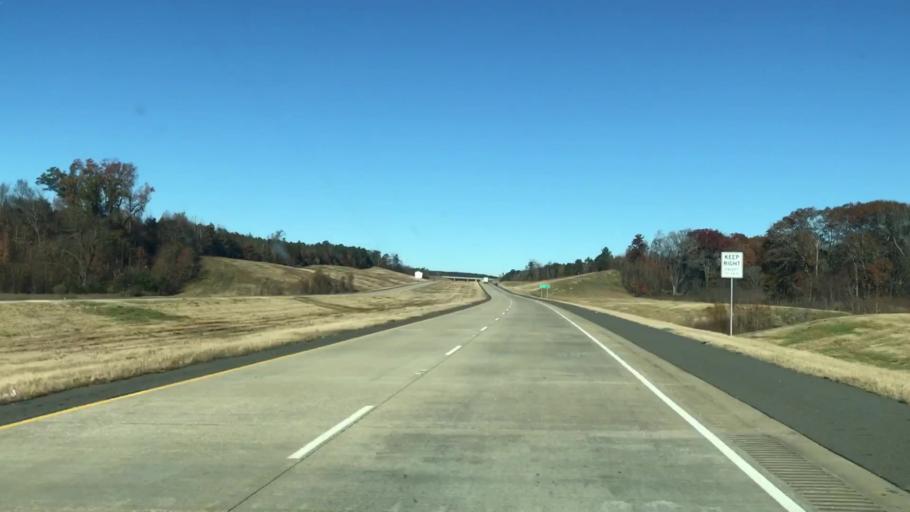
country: US
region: Louisiana
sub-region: Caddo Parish
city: Vivian
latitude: 32.9101
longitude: -93.8701
